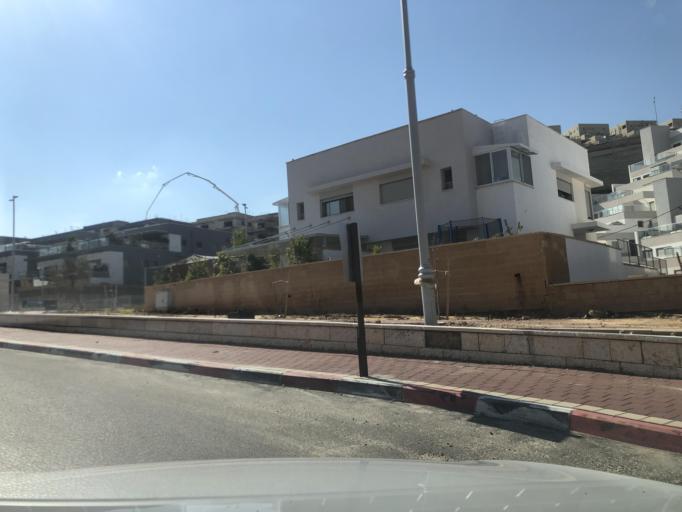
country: PS
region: West Bank
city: Mashah
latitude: 32.1125
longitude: 35.0428
